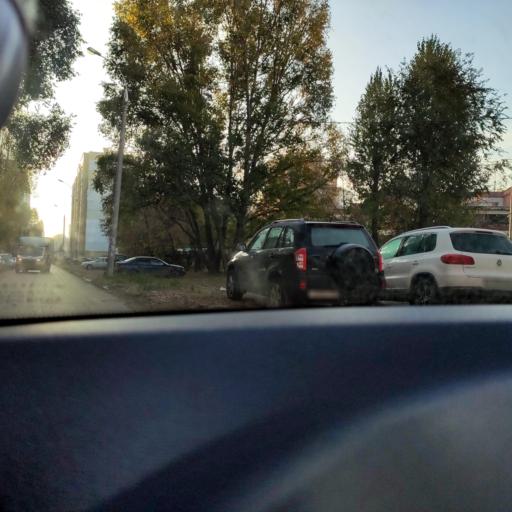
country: RU
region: Samara
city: Samara
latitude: 53.2375
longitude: 50.2525
